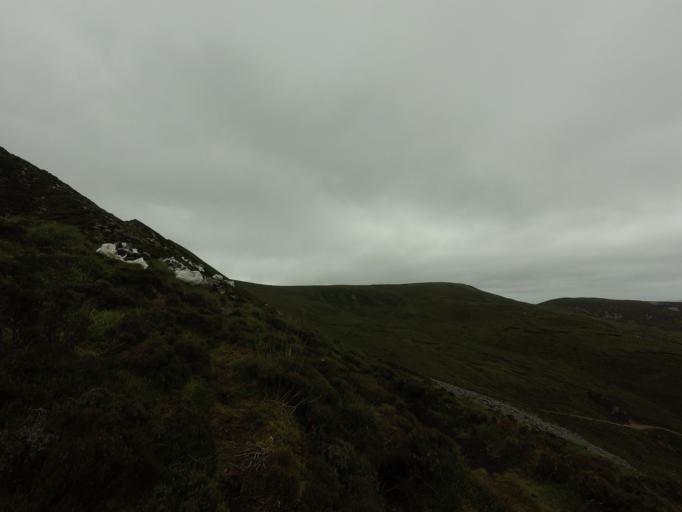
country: IE
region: Ulster
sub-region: County Donegal
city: Killybegs
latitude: 54.6427
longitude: -8.6851
